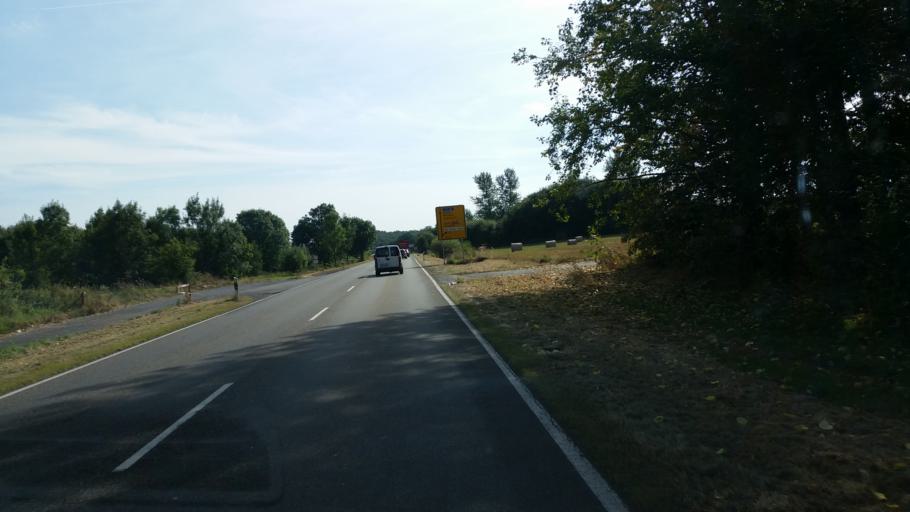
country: DE
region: Rheinland-Pfalz
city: Hartlingen
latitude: 50.5341
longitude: 7.8859
